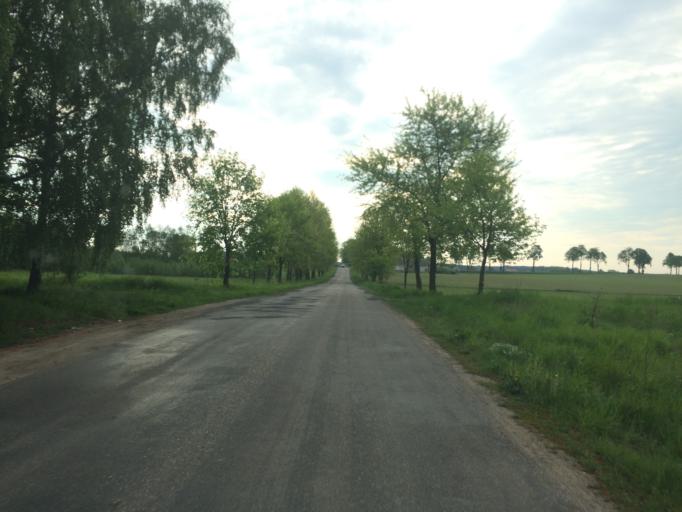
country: PL
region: Warmian-Masurian Voivodeship
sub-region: Powiat dzialdowski
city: Dzialdowo
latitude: 53.2883
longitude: 20.1338
